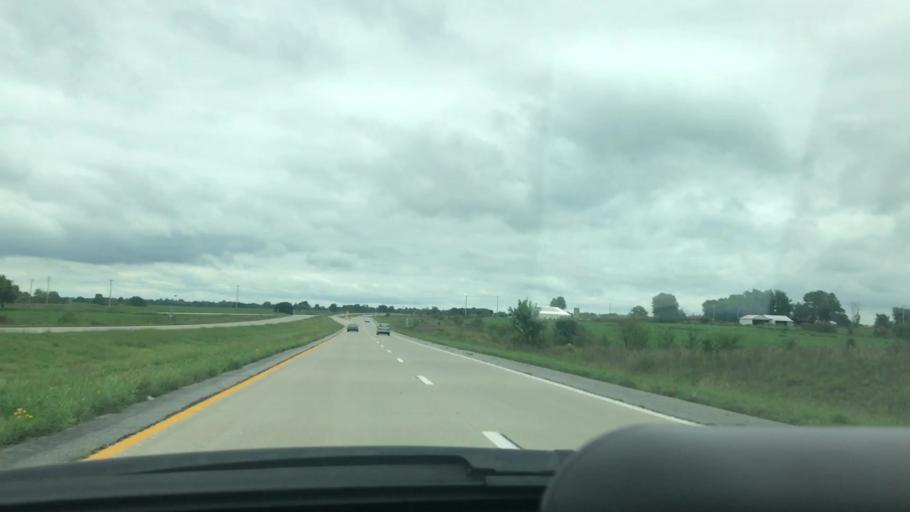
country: US
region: Missouri
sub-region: Dallas County
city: Buffalo
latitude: 37.6079
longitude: -93.1170
